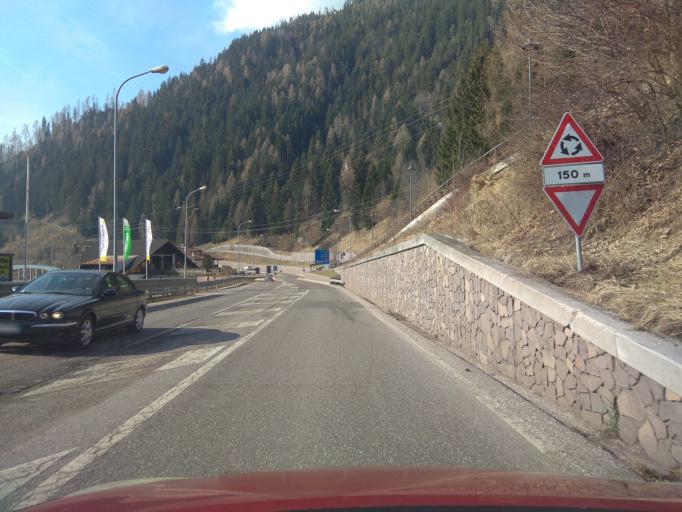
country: IT
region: Trentino-Alto Adige
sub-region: Provincia di Trento
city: Predazzo
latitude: 46.3207
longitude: 11.5966
